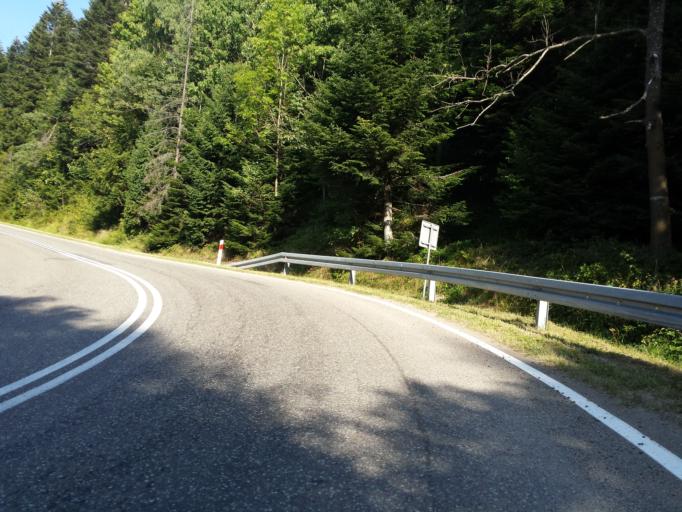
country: PL
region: Subcarpathian Voivodeship
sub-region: Powiat leski
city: Cisna
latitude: 49.2384
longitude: 22.3025
